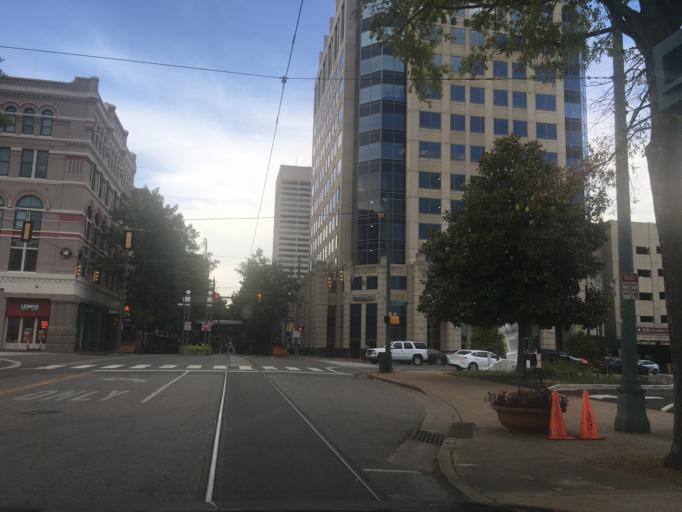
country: US
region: Tennessee
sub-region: Shelby County
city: Memphis
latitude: 35.1405
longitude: -90.0547
